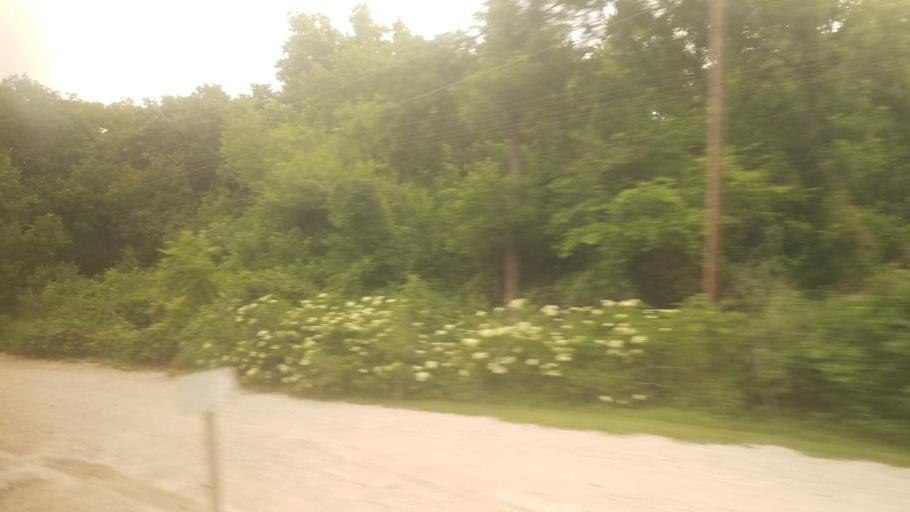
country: US
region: Kansas
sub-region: Osage County
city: Carbondale
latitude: 38.8843
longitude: -95.6952
